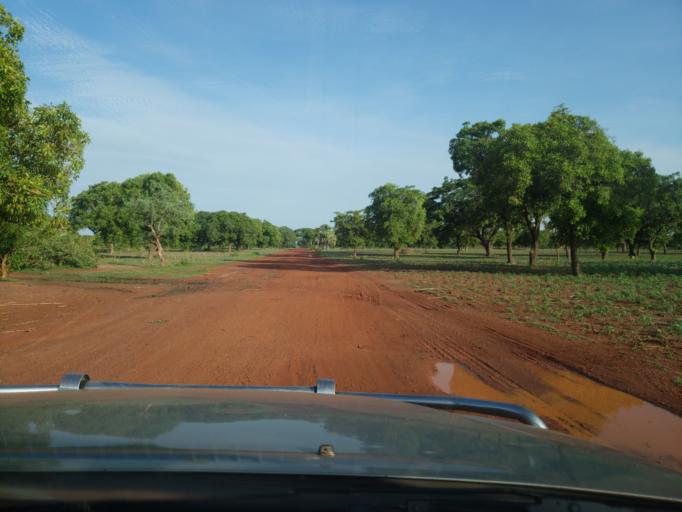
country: ML
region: Sikasso
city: Koutiala
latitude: 12.4246
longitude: -5.5930
